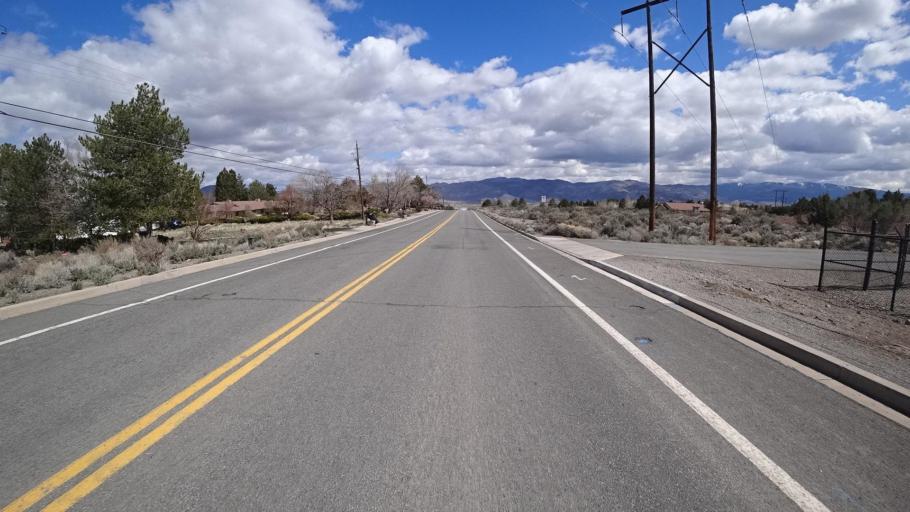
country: US
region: Nevada
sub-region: Washoe County
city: Reno
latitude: 39.4187
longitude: -119.7849
